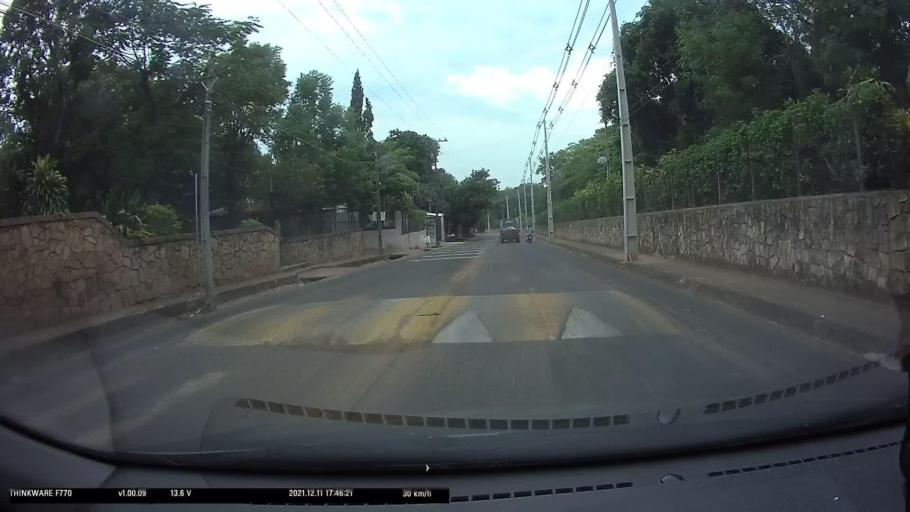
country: PY
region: Cordillera
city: San Bernardino
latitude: -25.2967
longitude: -57.2819
